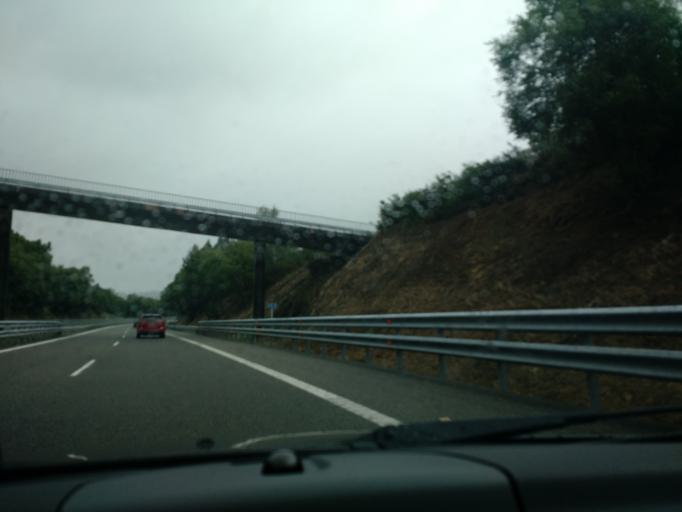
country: ES
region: Galicia
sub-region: Provincia da Coruna
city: Mesia
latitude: 43.1285
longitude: -8.3288
